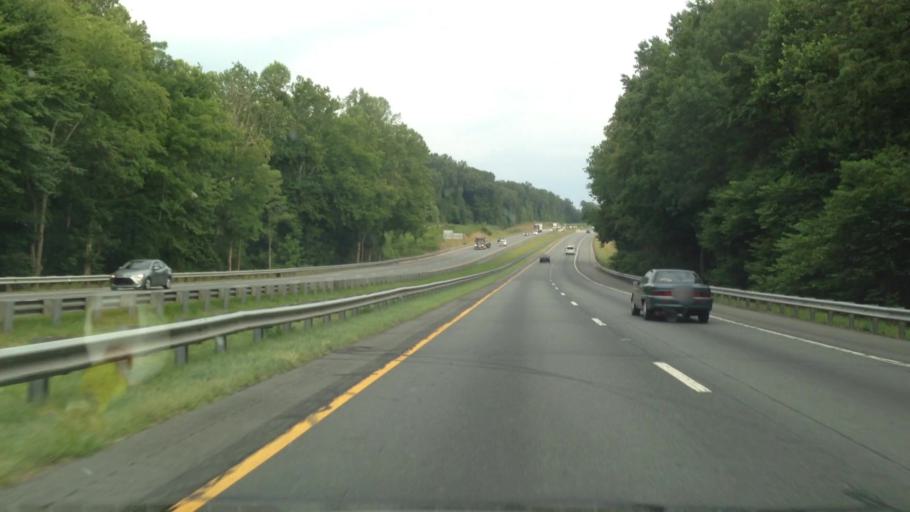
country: US
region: North Carolina
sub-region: Forsyth County
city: Tobaccoville
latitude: 36.2375
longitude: -80.3404
